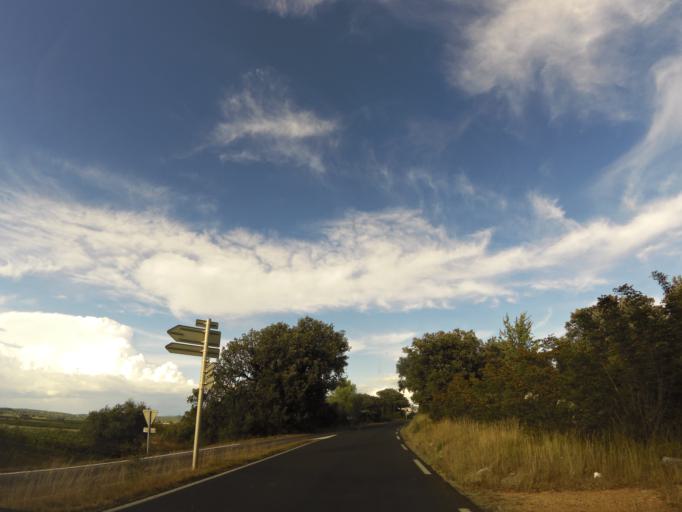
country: FR
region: Languedoc-Roussillon
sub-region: Departement de l'Herault
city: Boisseron
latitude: 43.7801
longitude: 4.0452
